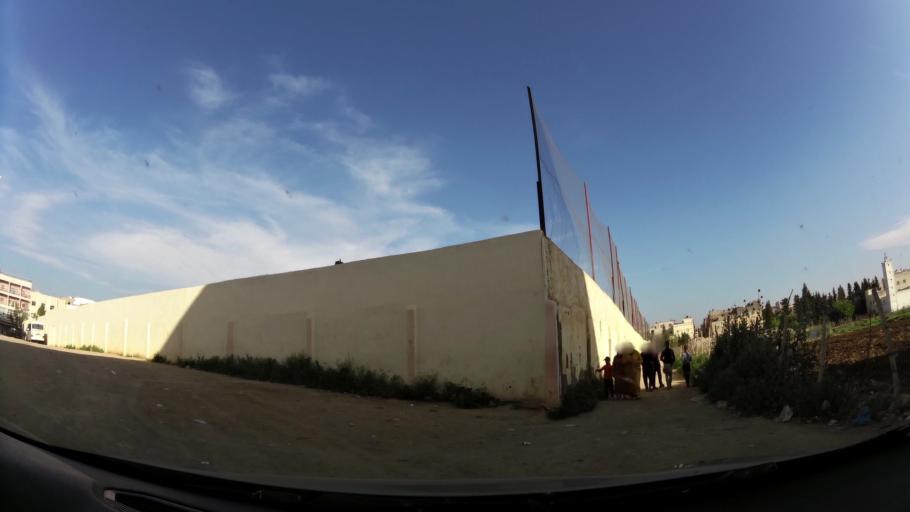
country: MA
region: Fes-Boulemane
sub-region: Fes
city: Fes
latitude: 34.0205
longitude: -5.0365
